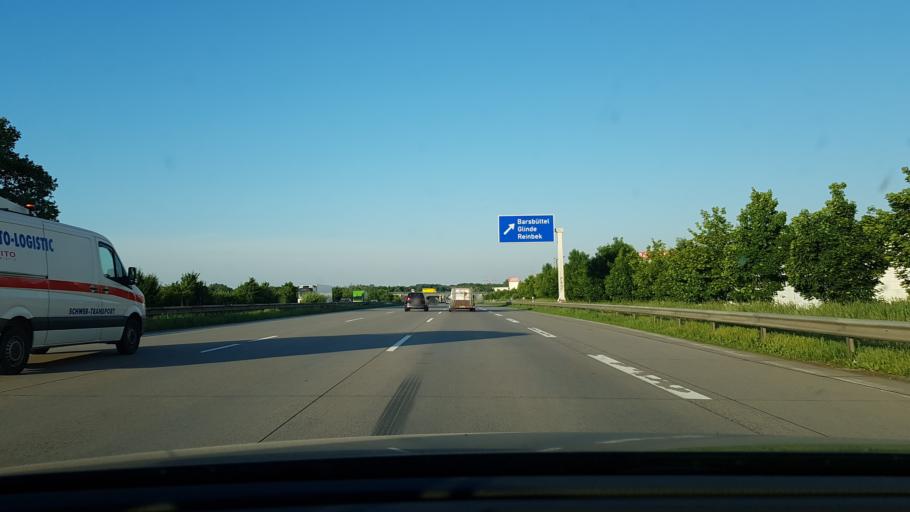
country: DE
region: Schleswig-Holstein
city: Stapelfeld
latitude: 53.5787
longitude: 10.2023
